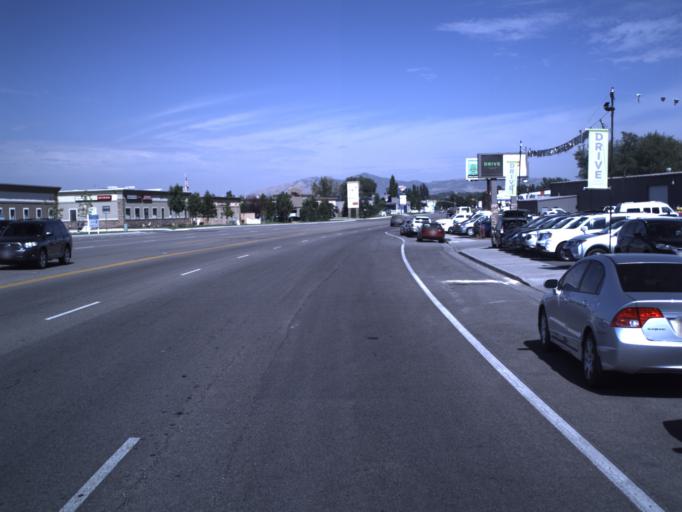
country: US
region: Utah
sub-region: Utah County
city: Pleasant Grove
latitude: 40.3615
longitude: -111.7474
